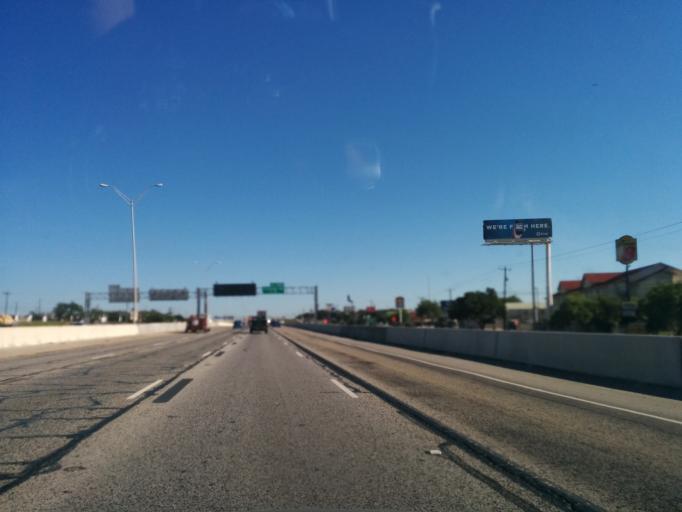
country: US
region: Texas
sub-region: Bexar County
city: Shavano Park
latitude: 29.5697
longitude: -98.5929
